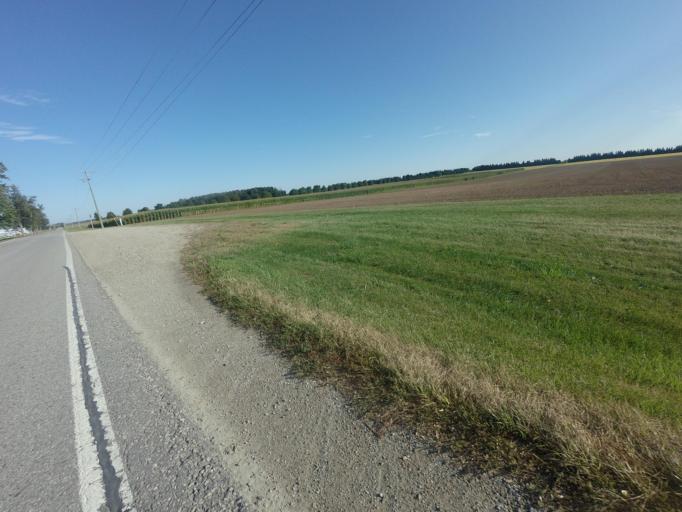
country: CA
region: Ontario
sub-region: Wellington County
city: Guelph
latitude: 43.6417
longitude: -80.4034
